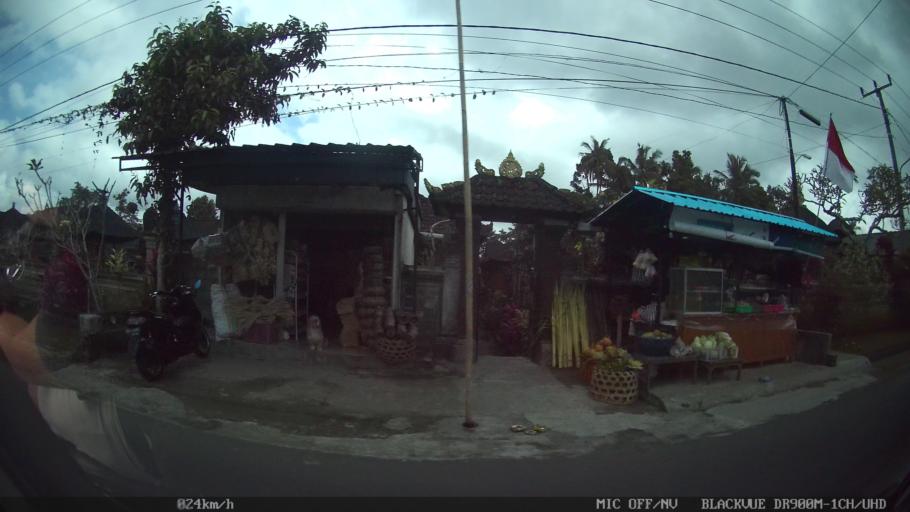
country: ID
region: Bali
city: Banjar Petak
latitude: -8.4455
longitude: 115.3190
